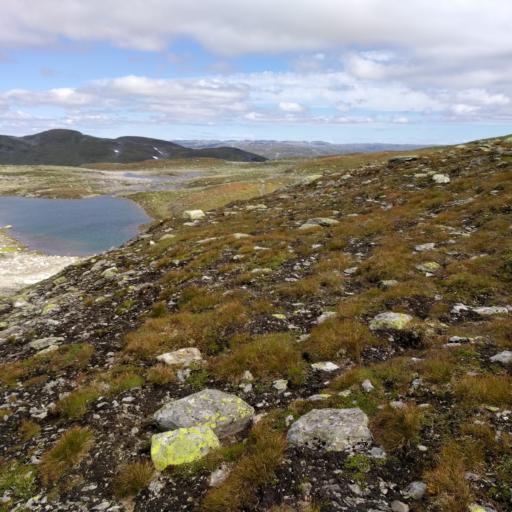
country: NO
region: Aust-Agder
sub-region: Bykle
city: Hovden
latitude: 59.8584
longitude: 7.2098
